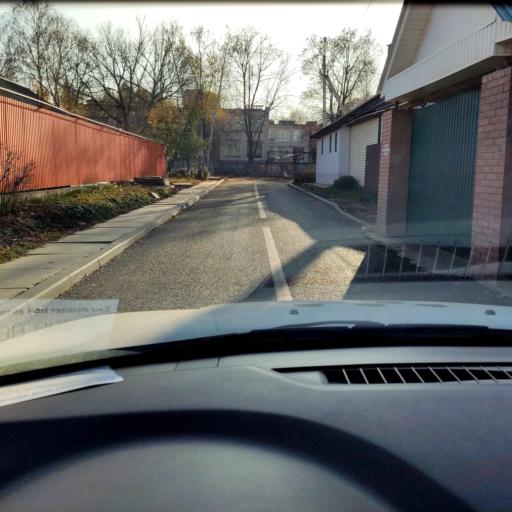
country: RU
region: Samara
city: Tol'yatti
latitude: 53.5263
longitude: 49.4197
